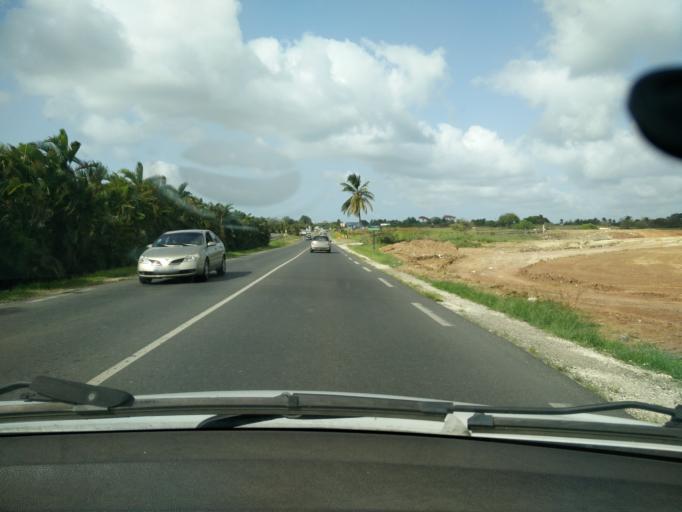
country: GP
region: Guadeloupe
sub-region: Guadeloupe
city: Les Abymes
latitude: 16.2613
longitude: -61.5163
